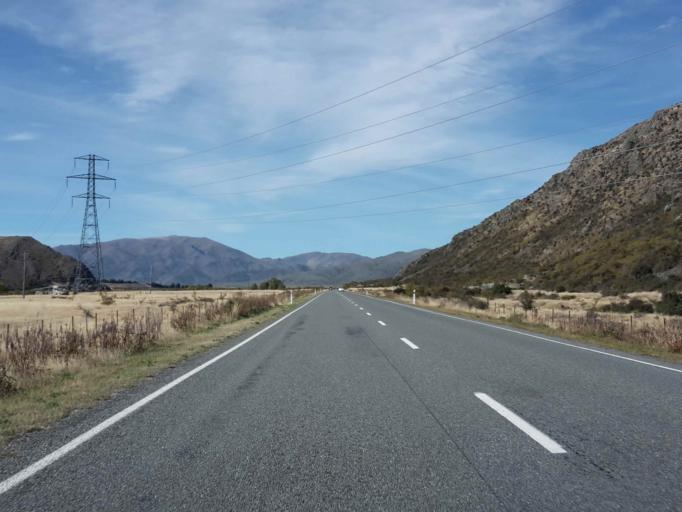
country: NZ
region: Otago
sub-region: Queenstown-Lakes District
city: Wanaka
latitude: -44.5018
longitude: 169.7710
